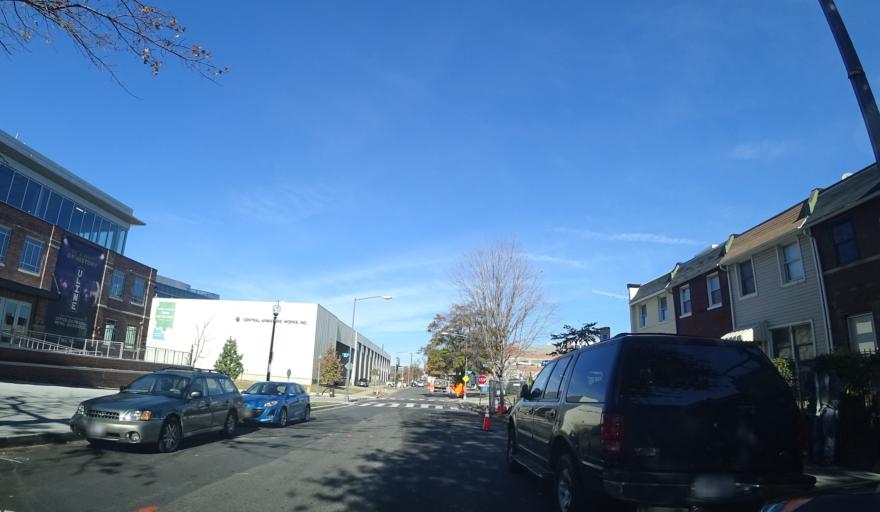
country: US
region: Washington, D.C.
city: Washington, D.C.
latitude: 38.9052
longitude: -77.0020
